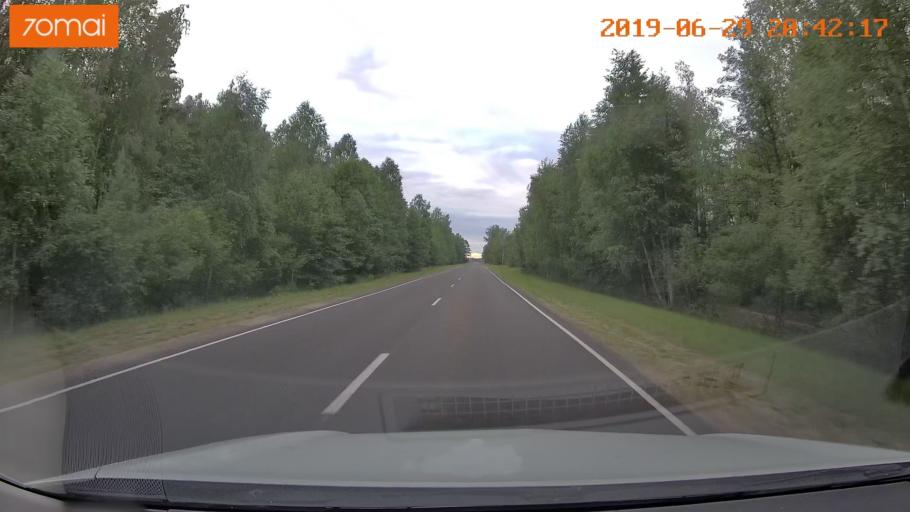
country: BY
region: Brest
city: Hantsavichy
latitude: 52.5958
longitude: 26.3283
